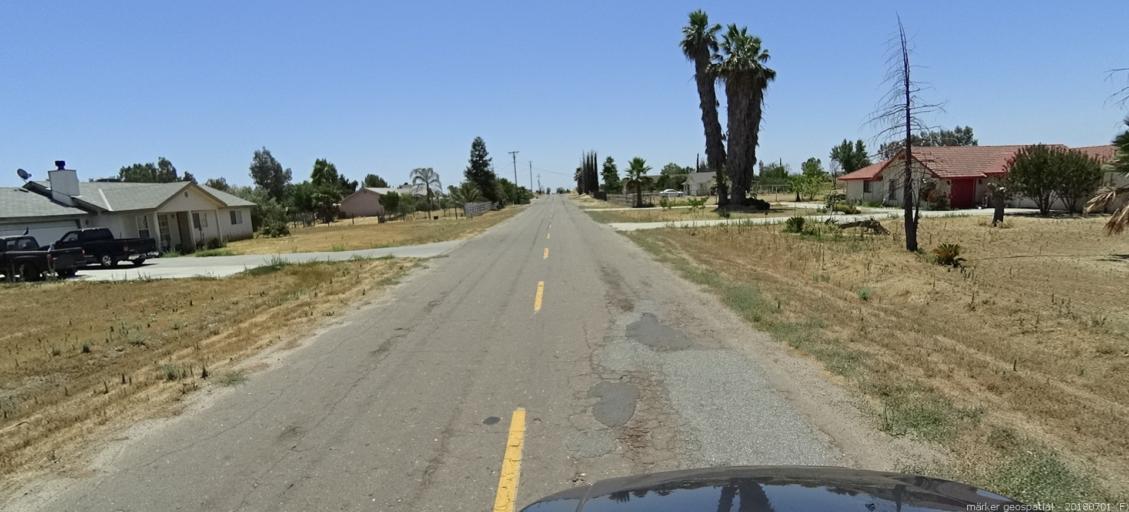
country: US
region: California
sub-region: Madera County
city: Madera Acres
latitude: 37.0421
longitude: -119.9988
